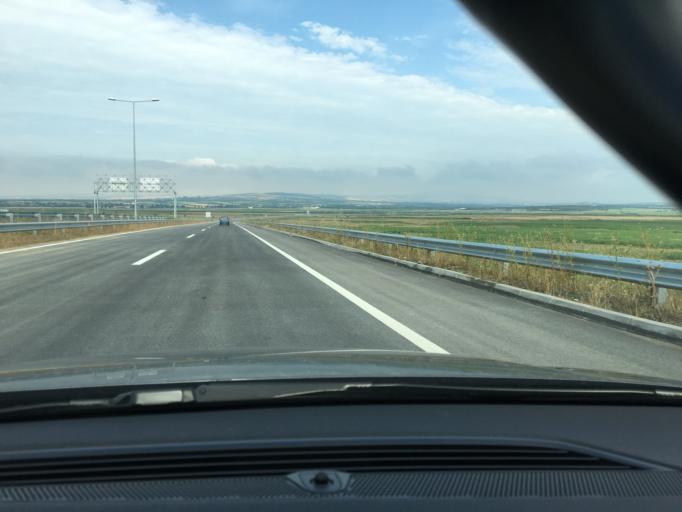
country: MK
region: Sveti Nikole
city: Sveti Nikole
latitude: 41.8128
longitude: 22.0304
